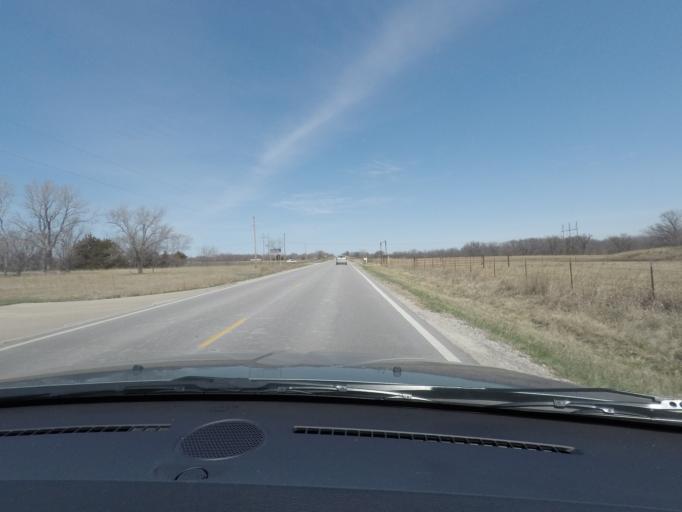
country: US
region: Kansas
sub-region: Lyon County
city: Emporia
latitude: 38.4803
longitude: -96.1710
